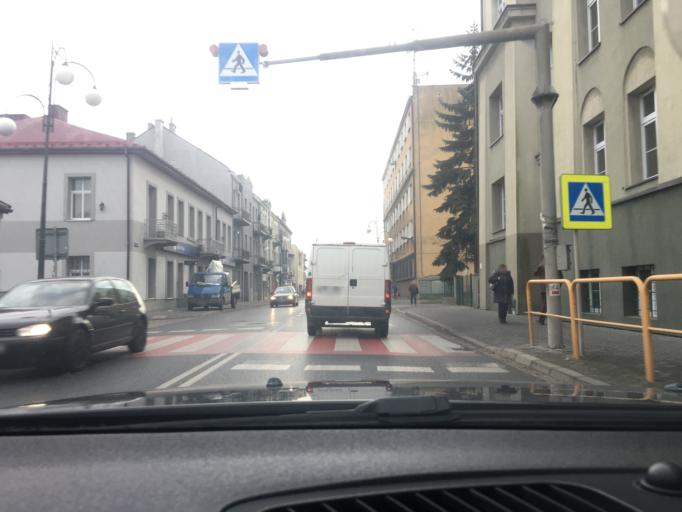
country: PL
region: Swietokrzyskie
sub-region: Powiat jedrzejowski
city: Jedrzejow
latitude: 50.6421
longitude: 20.2996
